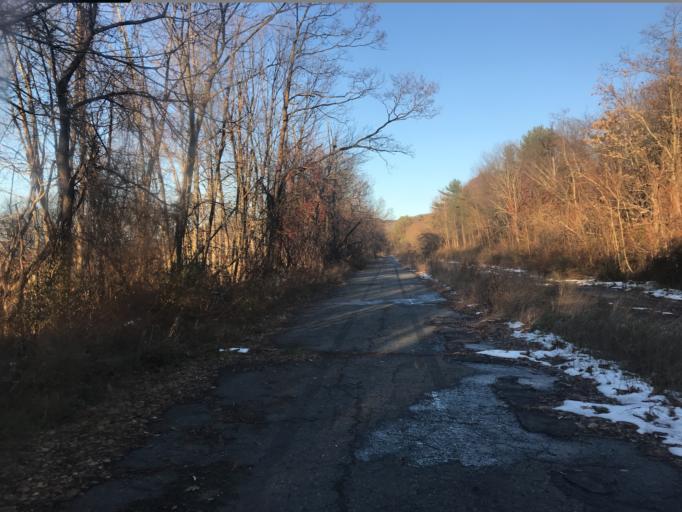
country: US
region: Pennsylvania
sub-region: Bedford County
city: Earlston
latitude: 40.0074
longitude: -78.2187
